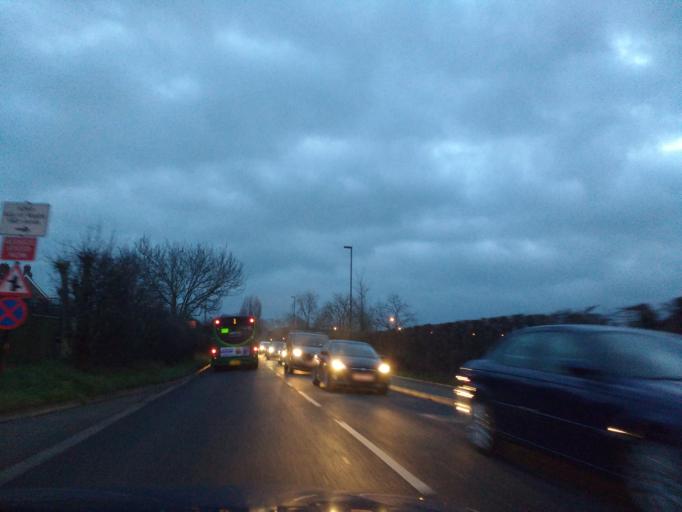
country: GB
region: England
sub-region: Isle of Wight
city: Newport
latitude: 50.7155
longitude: -1.3046
